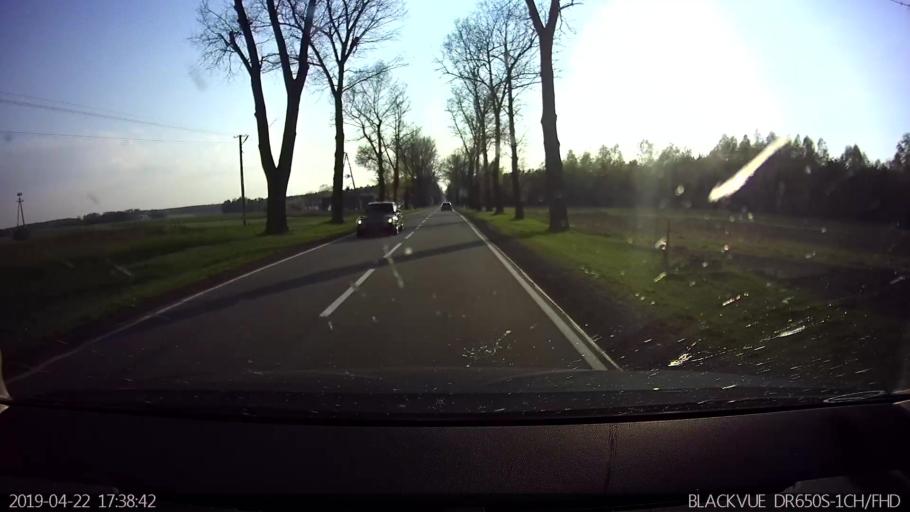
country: PL
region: Masovian Voivodeship
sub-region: Powiat wegrowski
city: Miedzna
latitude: 52.4072
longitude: 22.1563
